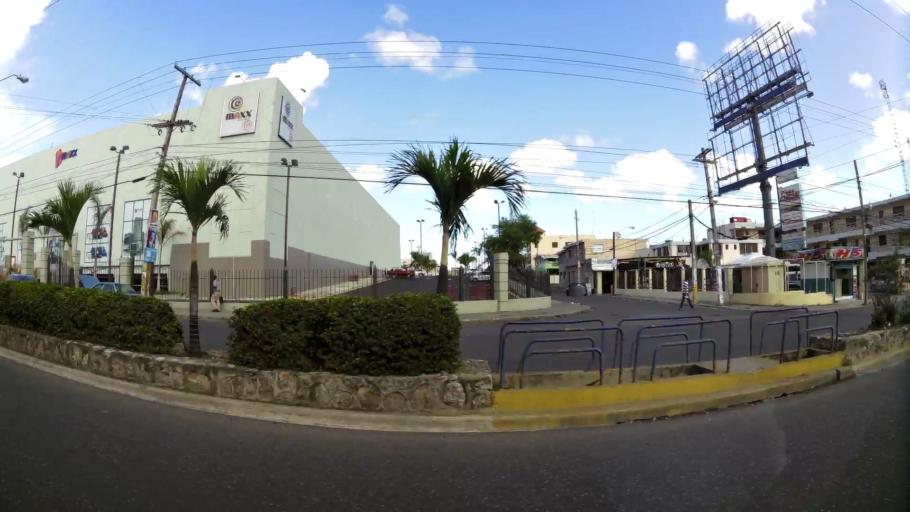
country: DO
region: Santo Domingo
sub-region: Santo Domingo
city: Santo Domingo Este
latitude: 18.5071
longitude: -69.8544
